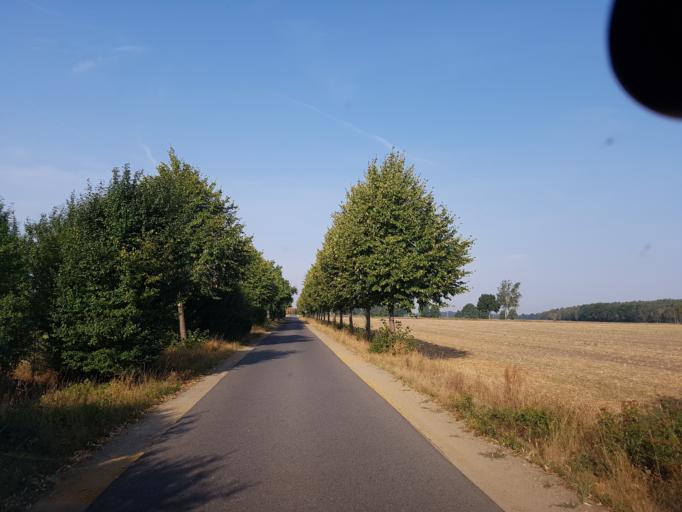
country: DE
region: Brandenburg
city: Finsterwalde
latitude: 51.6640
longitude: 13.6956
